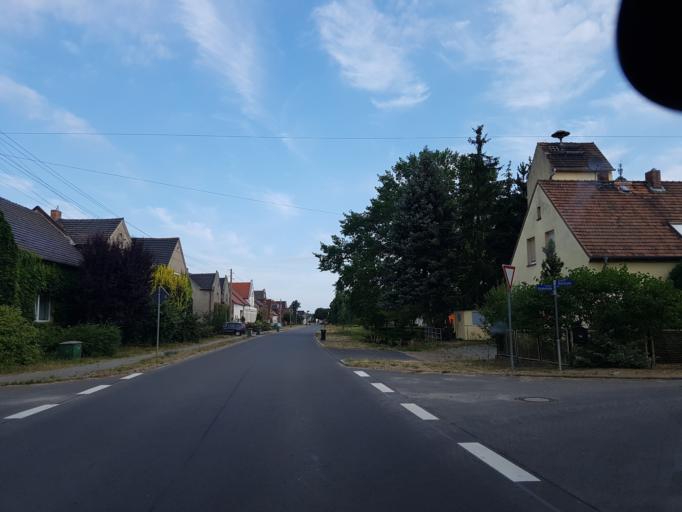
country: DE
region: Brandenburg
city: Luckau
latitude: 51.8371
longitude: 13.6404
